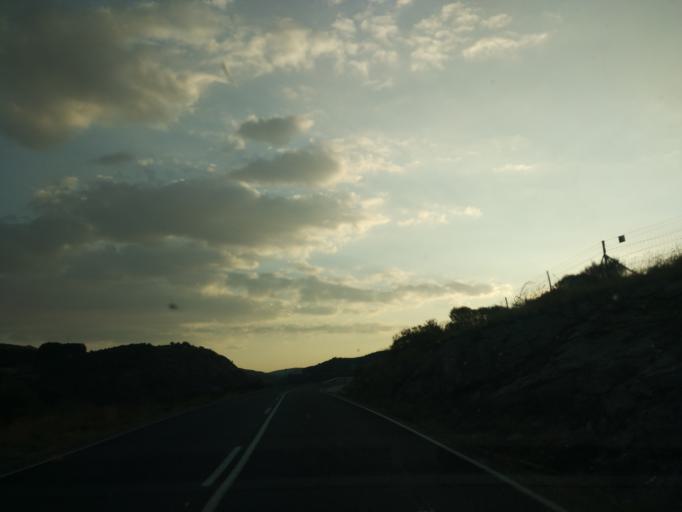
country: ES
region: Castille and Leon
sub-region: Provincia de Avila
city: San Martin del Pimpollar
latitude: 40.3731
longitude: -5.0282
